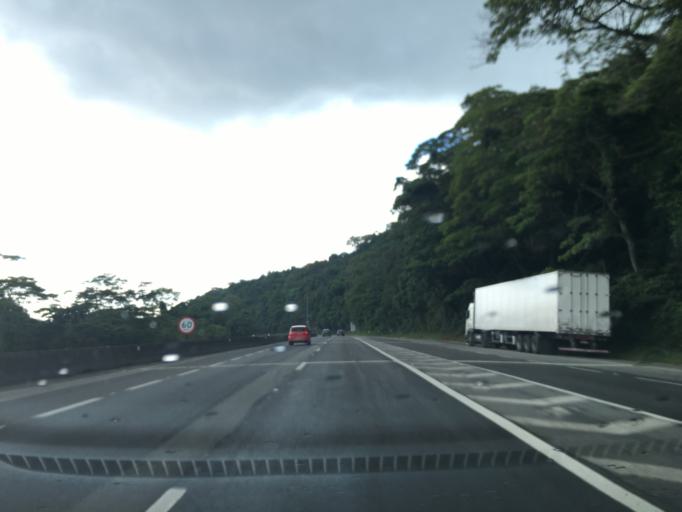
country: BR
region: Sao Paulo
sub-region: Mairipora
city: Mairipora
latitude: -23.3613
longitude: -46.5513
